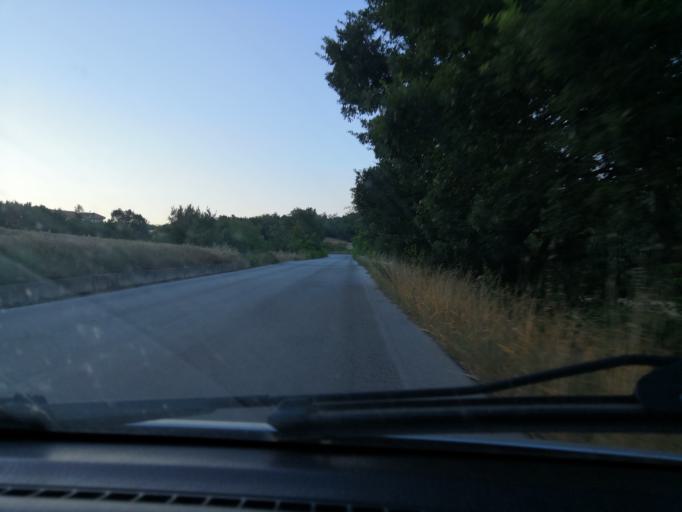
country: IT
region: Molise
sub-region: Provincia di Campobasso
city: Jelsi
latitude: 41.5123
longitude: 14.7747
